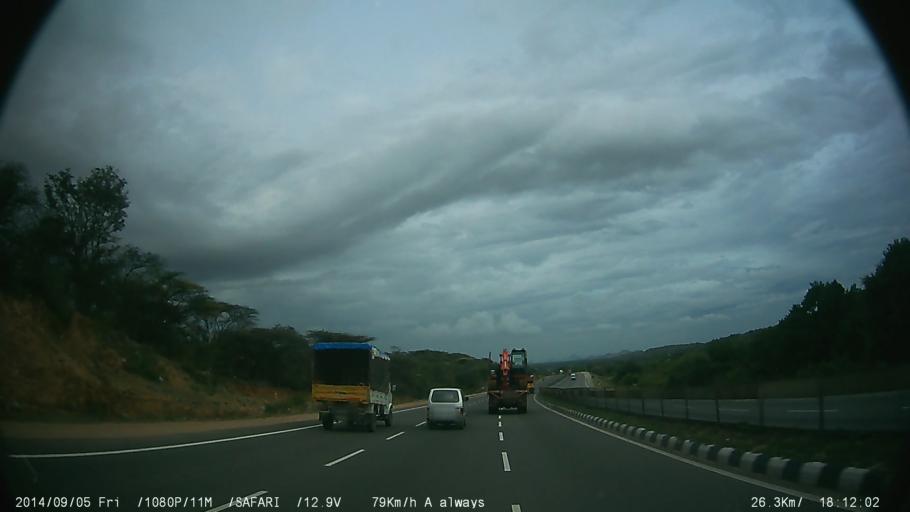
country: IN
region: Tamil Nadu
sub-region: Krishnagiri
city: Hosur
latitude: 12.6967
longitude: 77.9145
